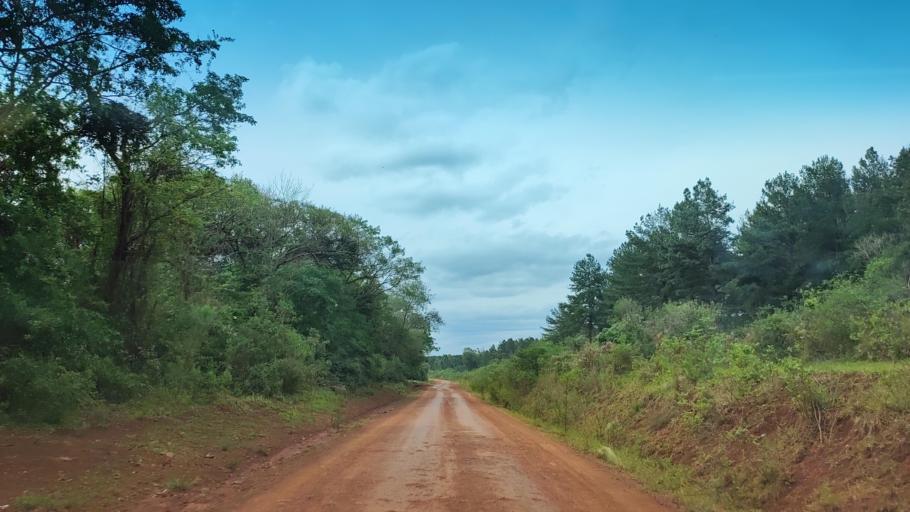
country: AR
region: Misiones
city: Garupa
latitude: -27.5087
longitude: -55.9703
